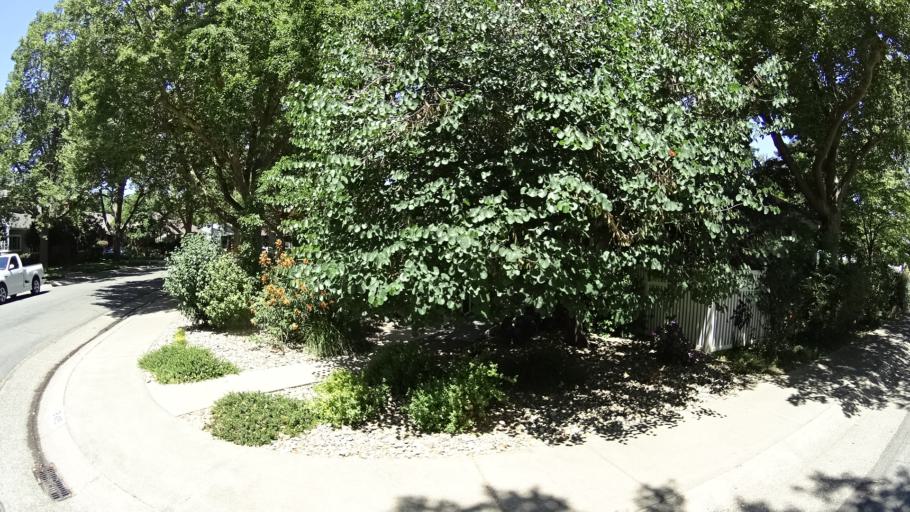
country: US
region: California
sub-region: Sacramento County
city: Sacramento
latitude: 38.5426
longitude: -121.5051
